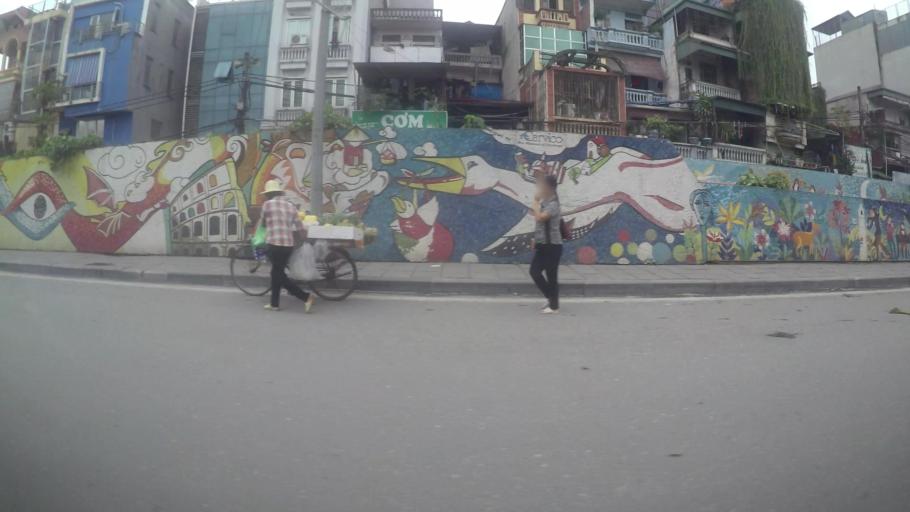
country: VN
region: Ha Noi
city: Hoan Kiem
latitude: 21.0393
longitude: 105.8518
